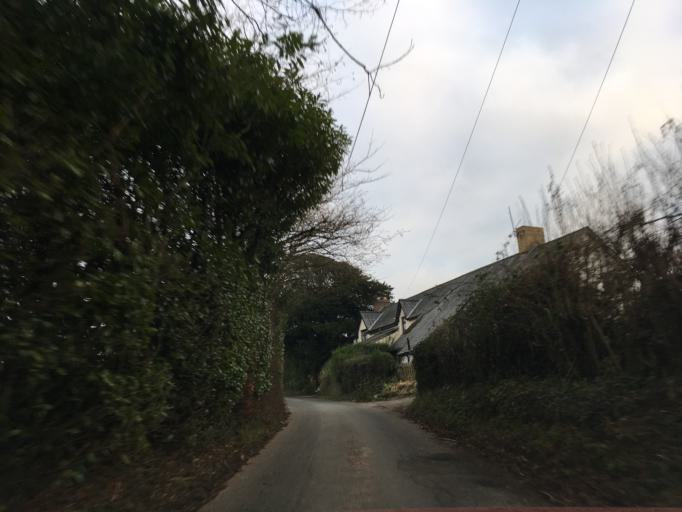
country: GB
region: Wales
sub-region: Newport
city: Marshfield
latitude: 51.5635
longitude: -3.0911
